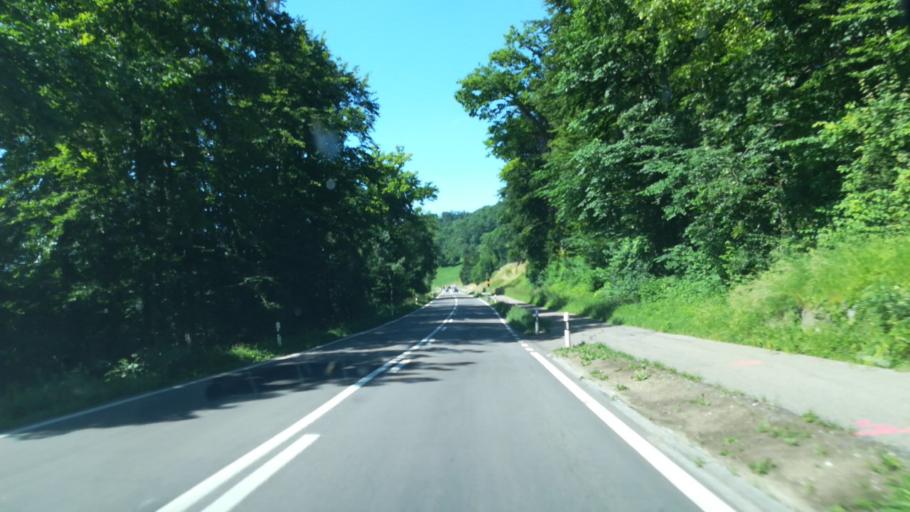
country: CH
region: Thurgau
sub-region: Weinfelden District
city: Sulgen
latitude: 47.5138
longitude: 9.2100
